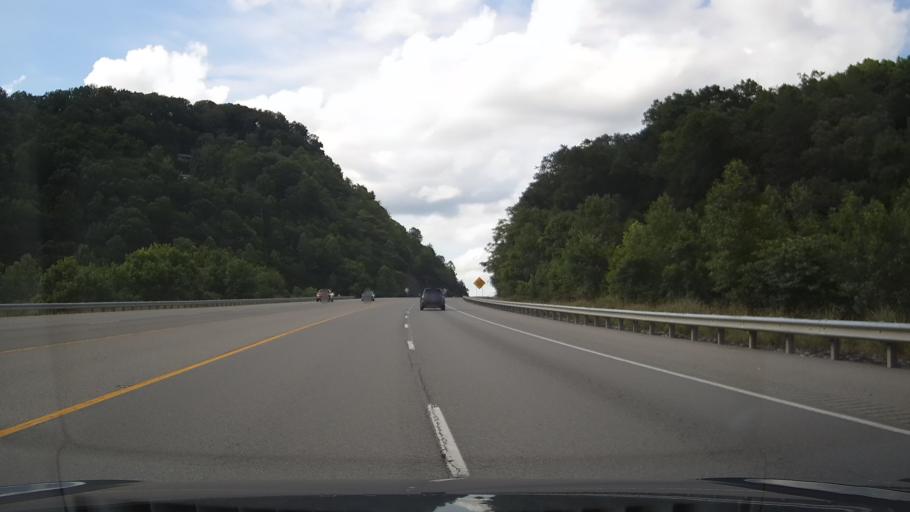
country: US
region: Kentucky
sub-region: Floyd County
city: Prestonsburg
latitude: 37.6906
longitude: -82.7909
